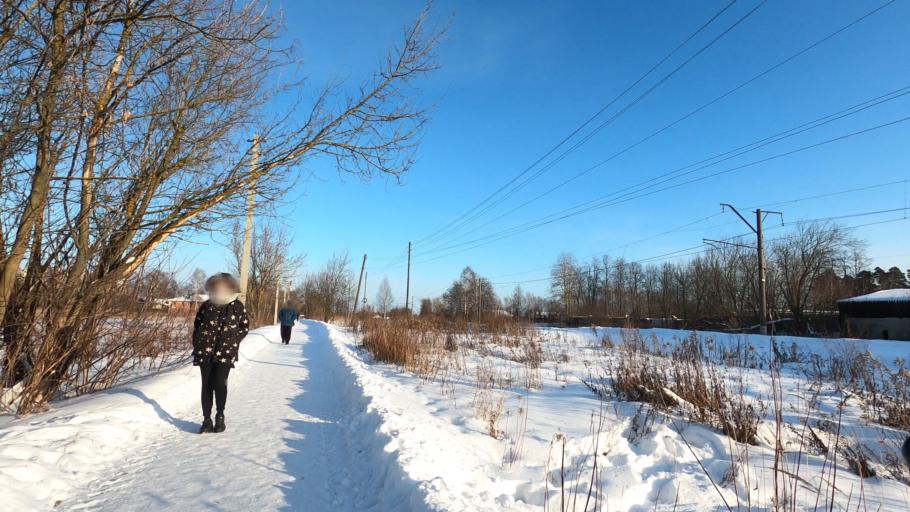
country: RU
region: Moskovskaya
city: Pavlovskiy Posad
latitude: 55.7748
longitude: 38.7039
